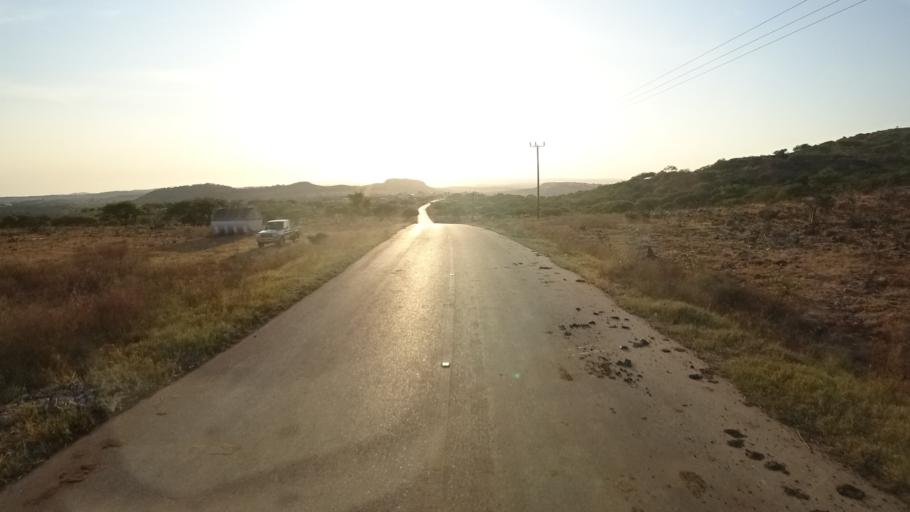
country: OM
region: Zufar
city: Salalah
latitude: 17.1487
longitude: 54.5981
